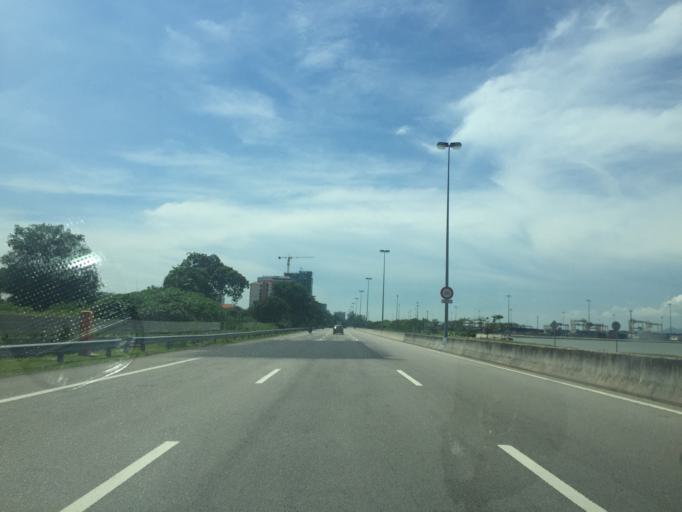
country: MY
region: Penang
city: Butterworth
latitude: 5.4244
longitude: 100.3747
